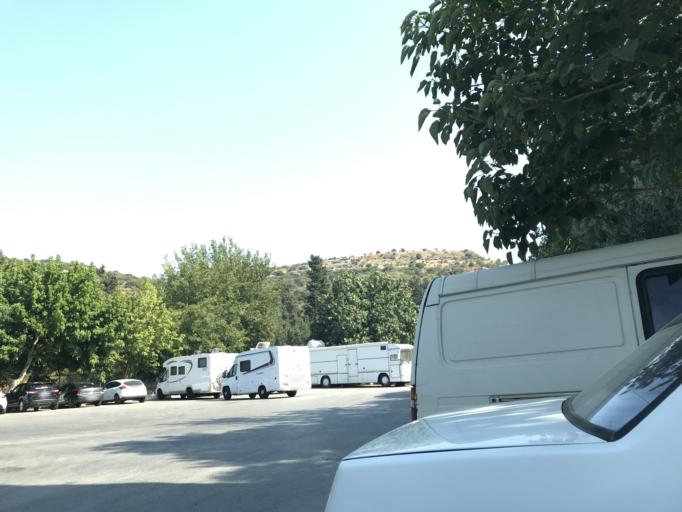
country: TR
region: Izmir
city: Selcuk
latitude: 37.9441
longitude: 27.3418
